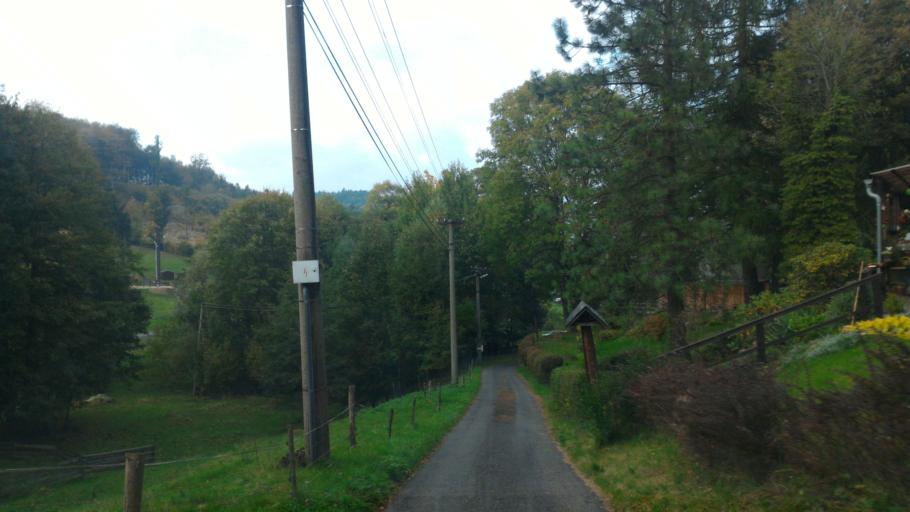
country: CZ
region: Ustecky
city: Dolni Podluzi
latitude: 50.8620
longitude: 14.5743
